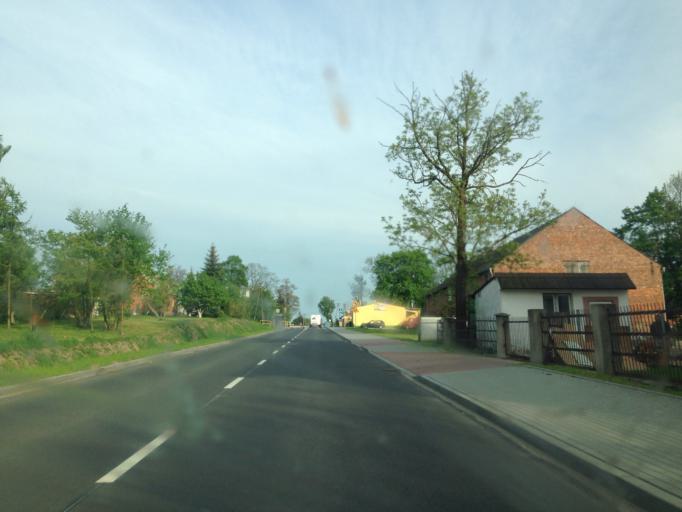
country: PL
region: Kujawsko-Pomorskie
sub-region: Powiat wabrzeski
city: Debowa Laka
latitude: 53.2587
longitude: 19.0933
